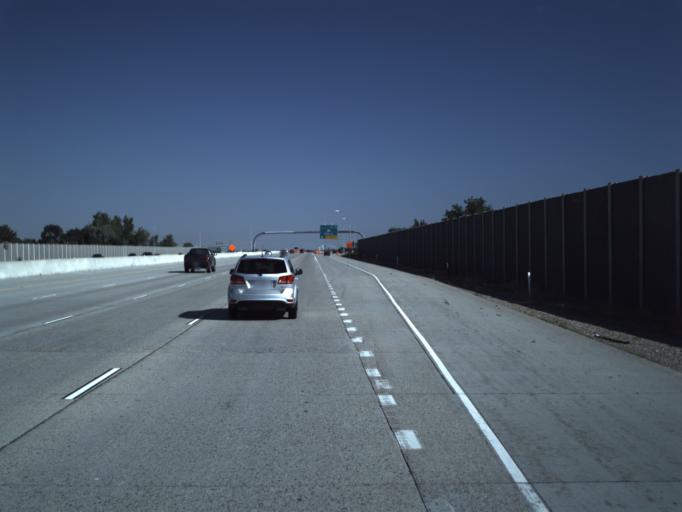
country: US
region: Utah
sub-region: Salt Lake County
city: Taylorsville
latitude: 40.6601
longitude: -111.9524
